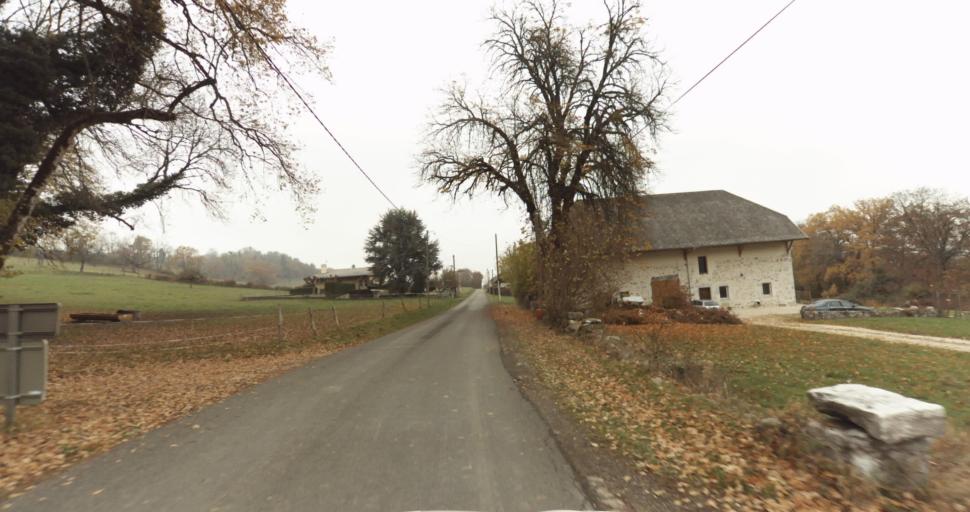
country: FR
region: Rhone-Alpes
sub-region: Departement de la Haute-Savoie
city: Cusy
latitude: 45.7797
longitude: 6.0104
